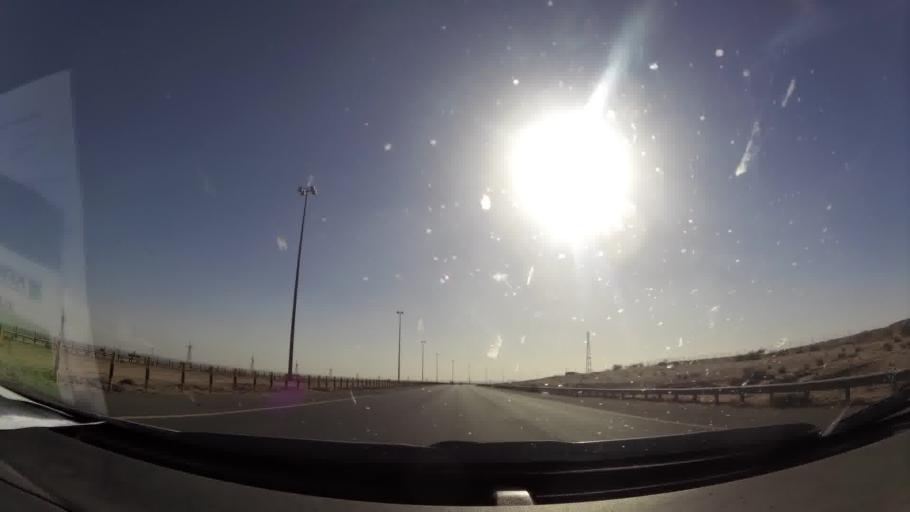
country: KW
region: Muhafazat al Jahra'
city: Al Jahra'
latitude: 29.4540
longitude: 47.7582
